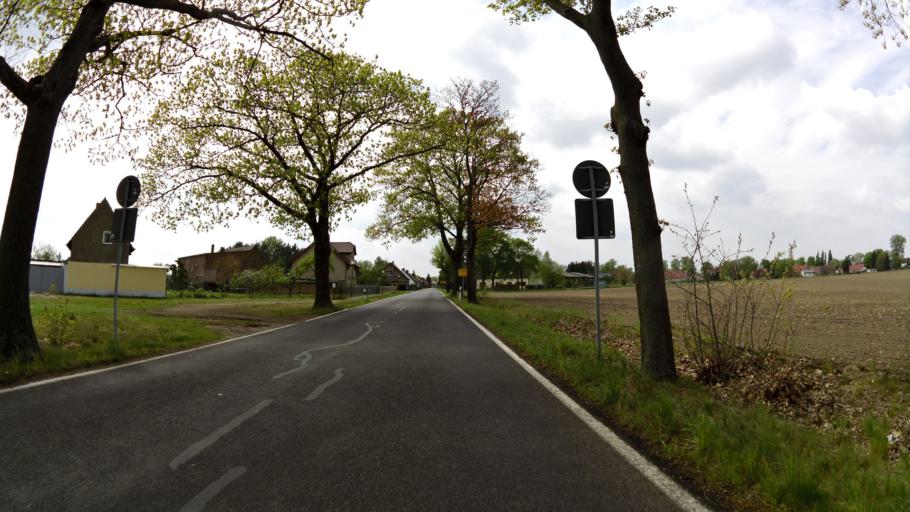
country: DE
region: Brandenburg
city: Bestensee
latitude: 52.2433
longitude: 13.7132
